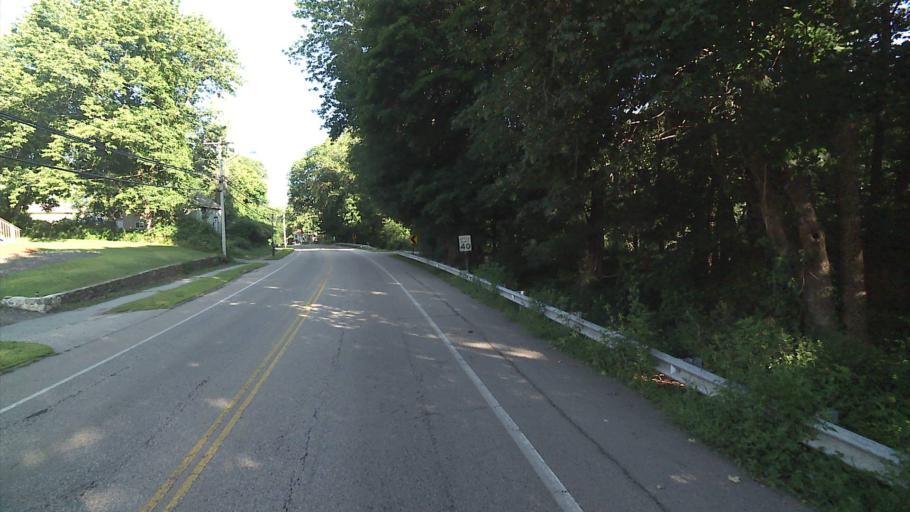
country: US
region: Connecticut
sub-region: New London County
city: Central Waterford
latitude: 41.3554
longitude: -72.1658
